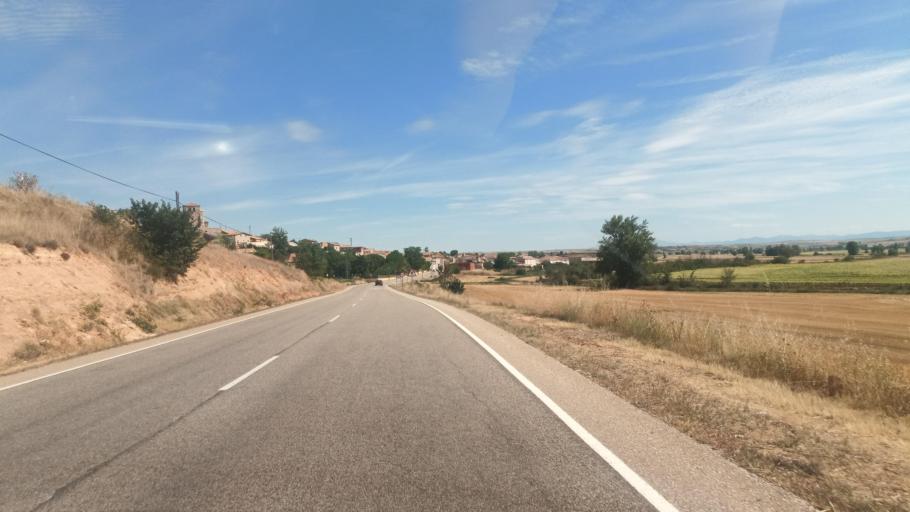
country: ES
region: Castille and Leon
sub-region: Provincia de Burgos
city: Quintanabureba
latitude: 42.6201
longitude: -3.3654
